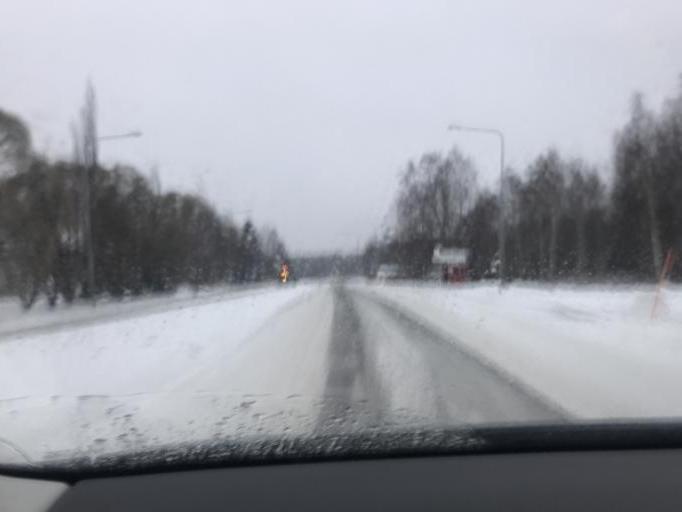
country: SE
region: Norrbotten
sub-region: Lulea Kommun
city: Sodra Sunderbyn
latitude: 65.6532
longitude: 21.9654
